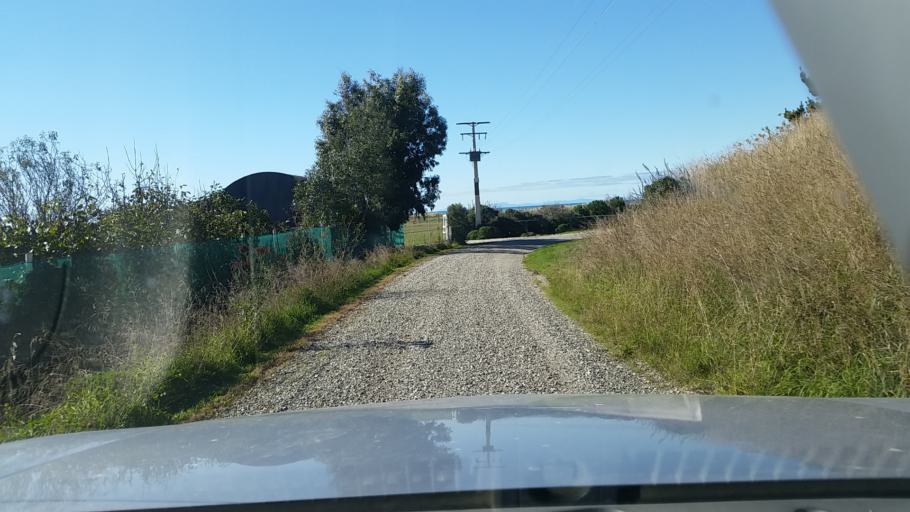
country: NZ
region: Marlborough
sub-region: Marlborough District
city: Blenheim
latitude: -41.6651
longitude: 174.1568
